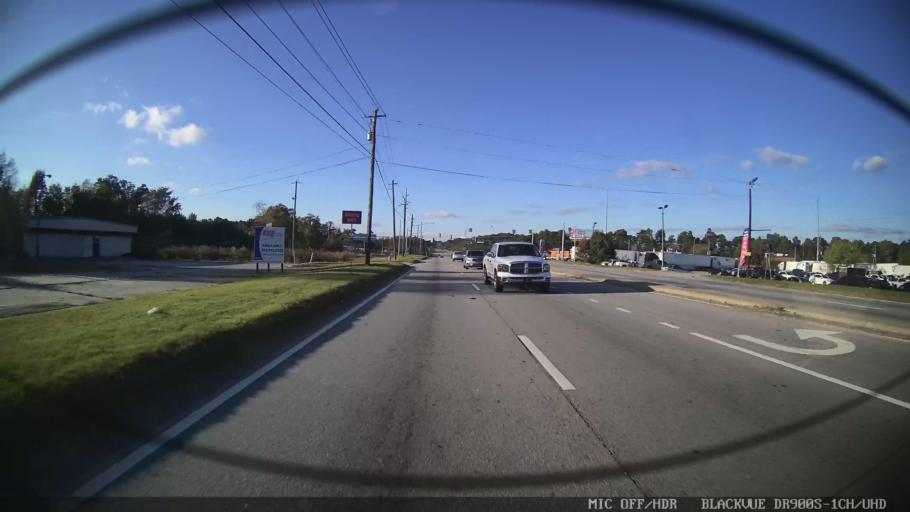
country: US
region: Georgia
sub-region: Clayton County
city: Conley
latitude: 33.6565
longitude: -84.3346
